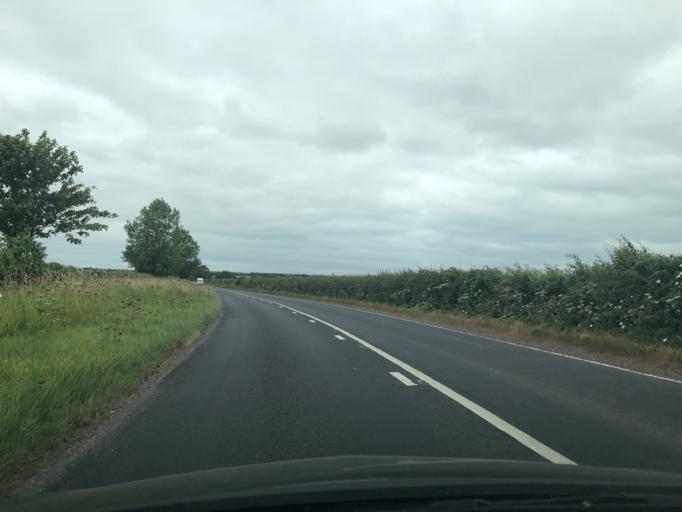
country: GB
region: England
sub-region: North Yorkshire
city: East Ayton
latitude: 54.2490
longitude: -0.4611
